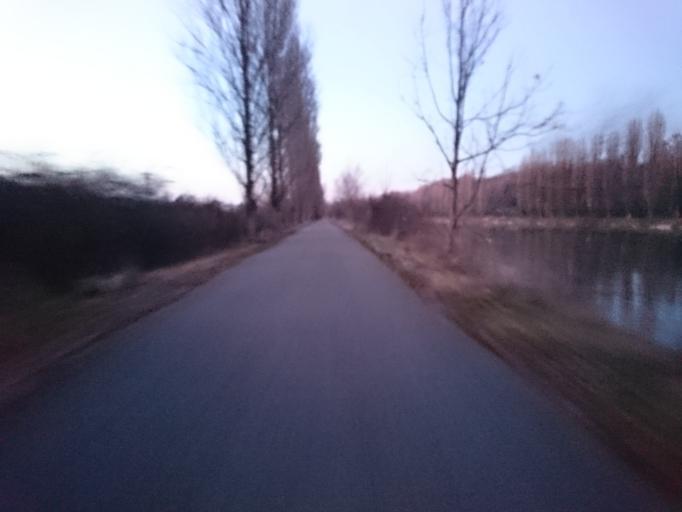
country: IT
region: Veneto
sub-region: Provincia di Verona
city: Salionze
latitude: 45.4108
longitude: 10.7164
